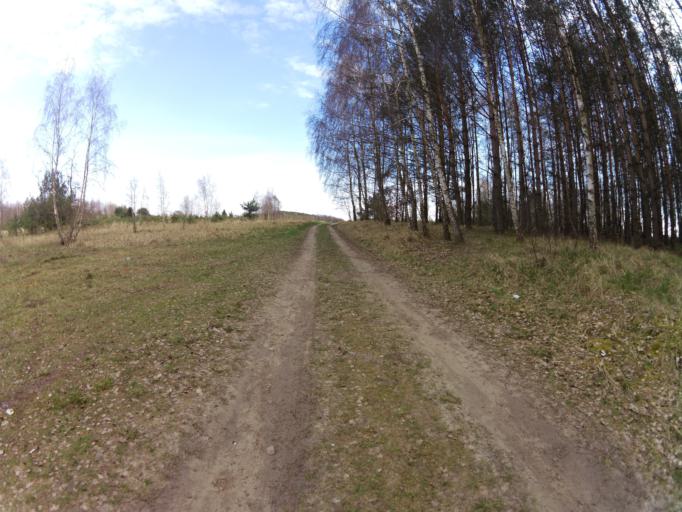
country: PL
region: West Pomeranian Voivodeship
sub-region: Powiat mysliborski
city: Mysliborz
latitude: 52.9610
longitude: 14.8811
